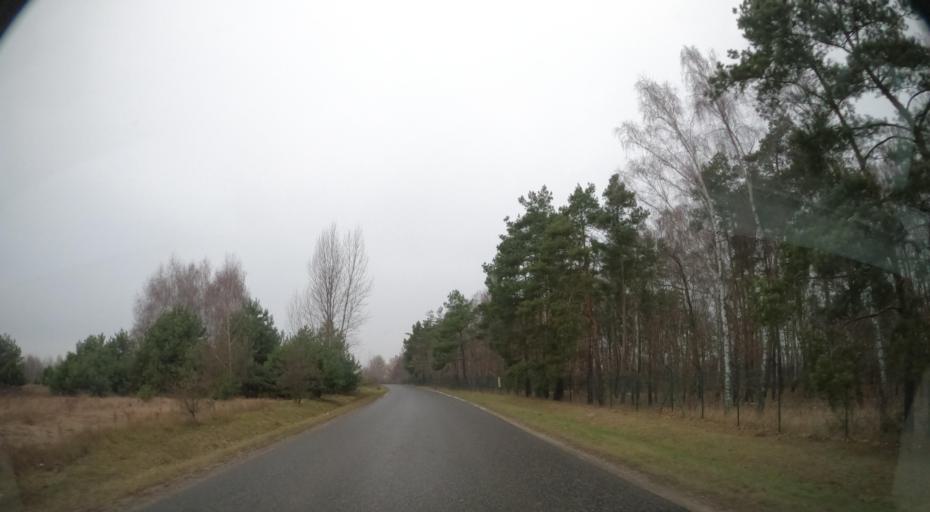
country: PL
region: Masovian Voivodeship
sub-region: Radom
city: Radom
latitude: 51.3830
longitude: 21.2148
